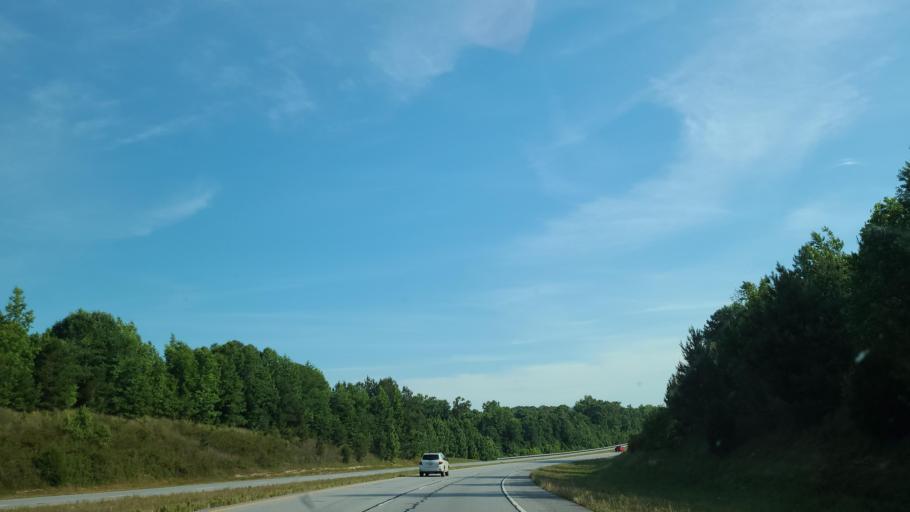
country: US
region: Georgia
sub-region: Jackson County
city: Nicholson
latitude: 34.0641
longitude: -83.4258
